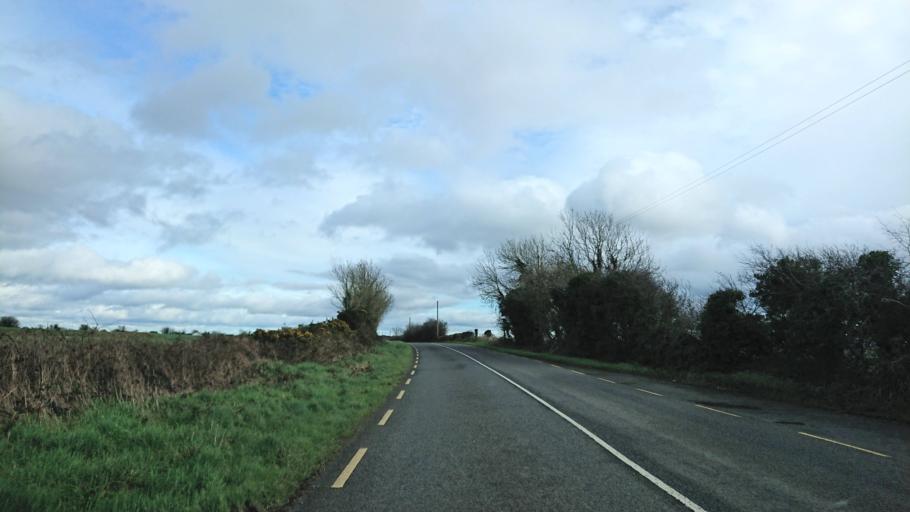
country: IE
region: Munster
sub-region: Waterford
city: Dunmore East
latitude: 52.2411
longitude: -6.8862
